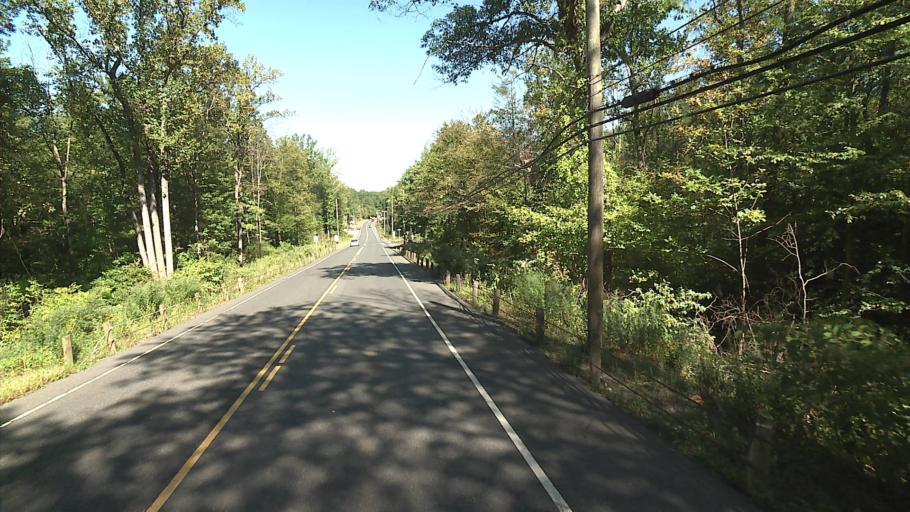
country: US
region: Connecticut
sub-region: New Haven County
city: Prospect
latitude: 41.5043
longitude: -72.9482
